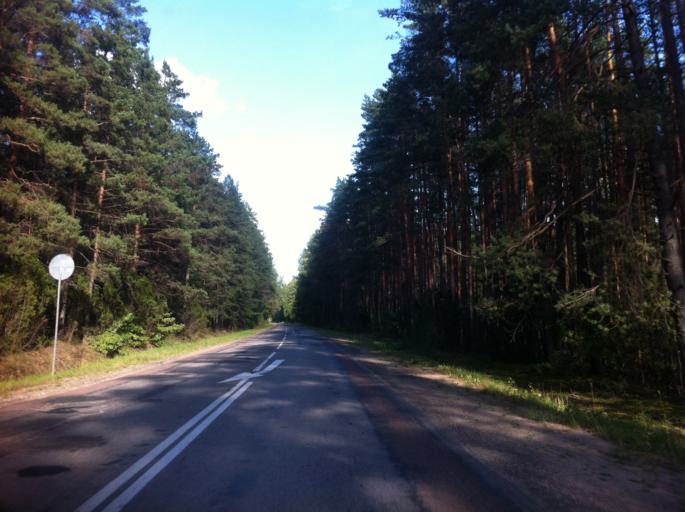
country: RU
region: Pskov
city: Izborsk
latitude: 57.8024
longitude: 27.7810
